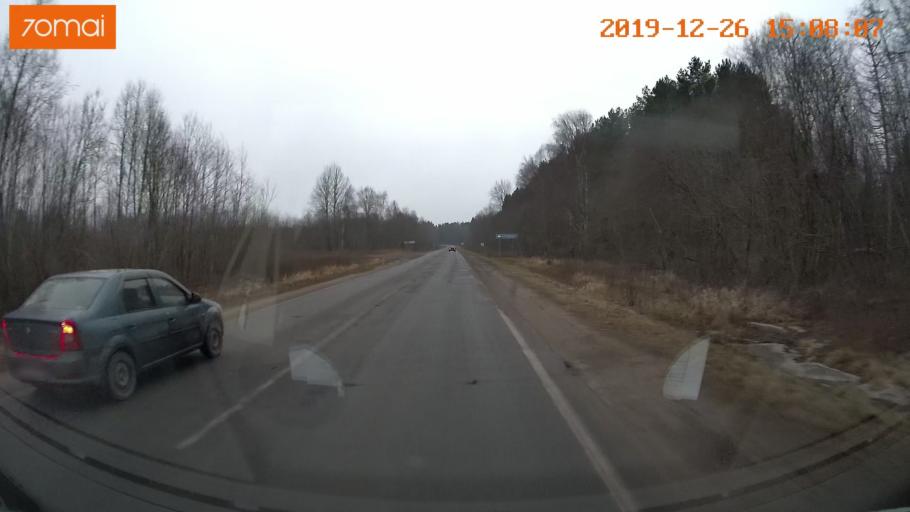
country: RU
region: Jaroslavl
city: Rybinsk
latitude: 58.1631
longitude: 38.8403
